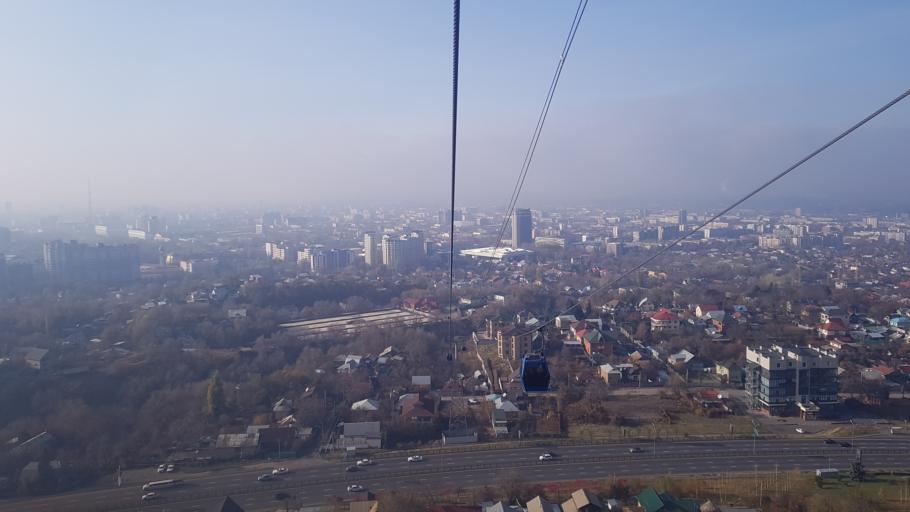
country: KZ
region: Almaty Qalasy
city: Almaty
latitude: 43.2355
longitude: 76.9730
